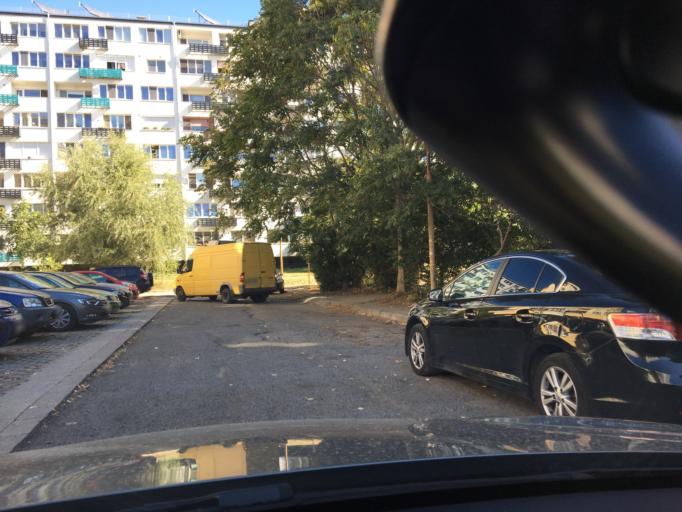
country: BG
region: Burgas
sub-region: Obshtina Burgas
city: Burgas
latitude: 42.5170
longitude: 27.4501
